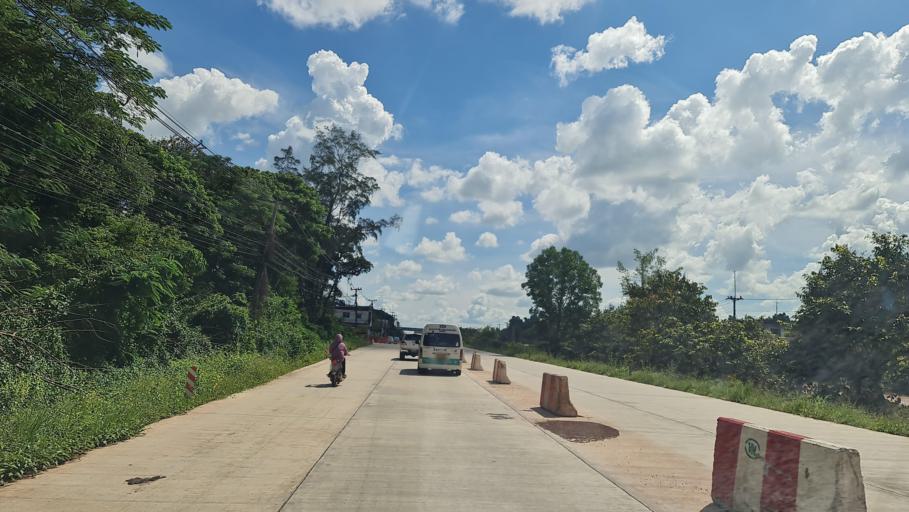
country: TH
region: Nong Khai
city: Sa Khrai
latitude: 17.6670
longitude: 102.7909
